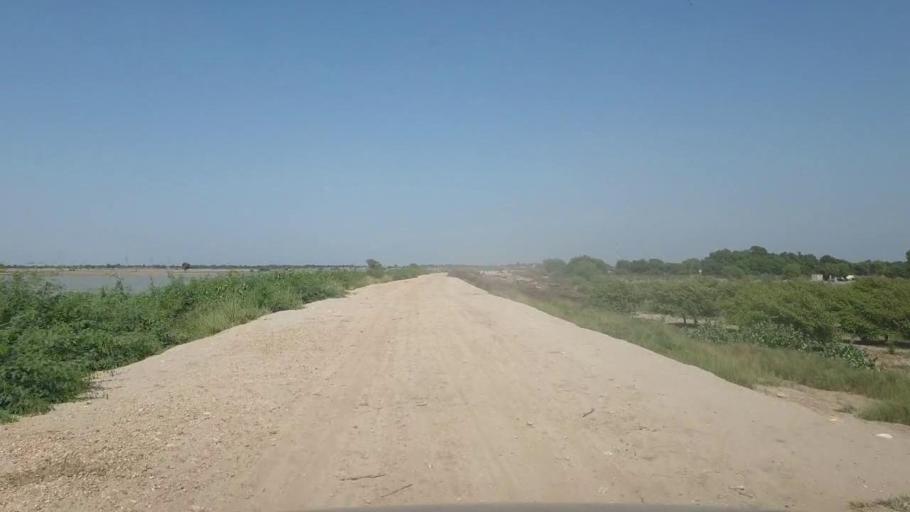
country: PK
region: Sindh
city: Matiari
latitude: 25.6389
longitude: 68.4867
